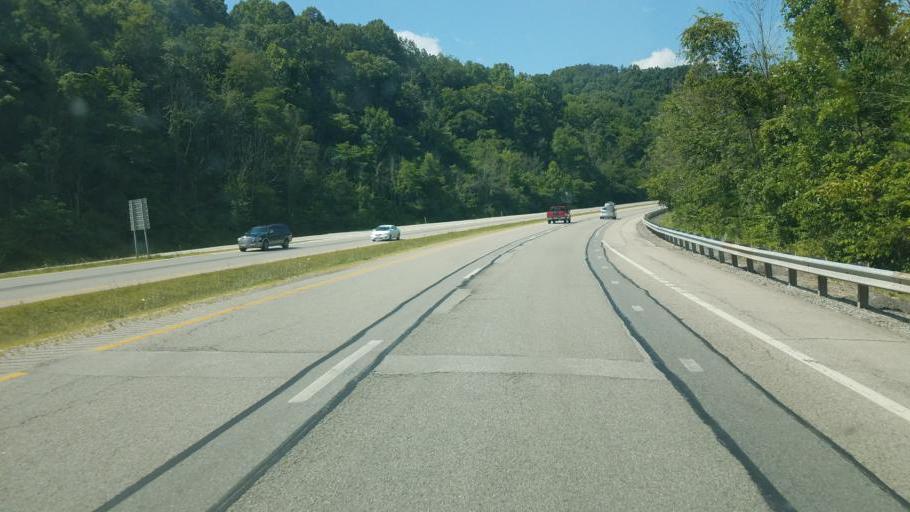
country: US
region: West Virginia
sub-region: Kanawha County
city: Sissonville
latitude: 38.4644
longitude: -81.6451
